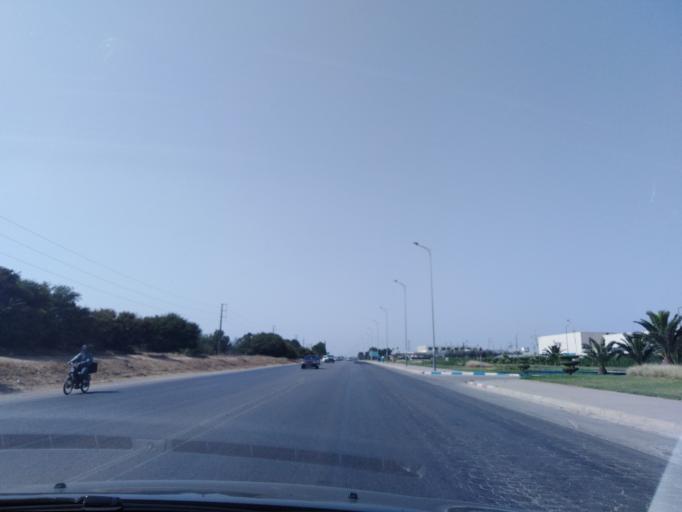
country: MA
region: Chaouia-Ouardigha
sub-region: Settat Province
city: Berrechid
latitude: 33.2504
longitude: -7.5848
